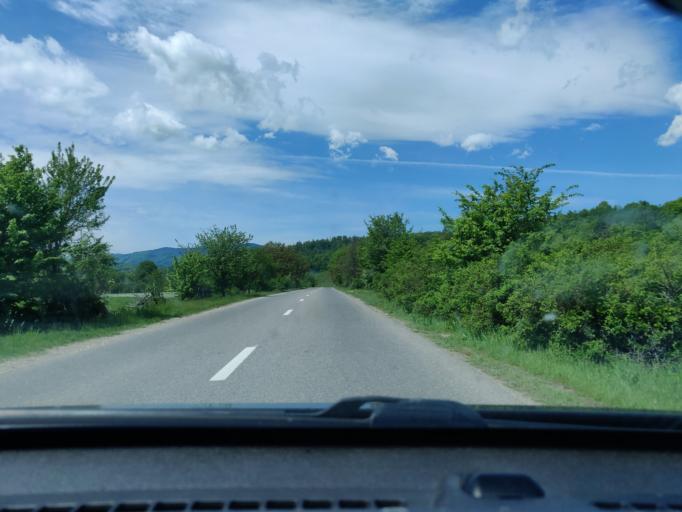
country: RO
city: Campurile de Jos
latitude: 46.0421
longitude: 26.7254
